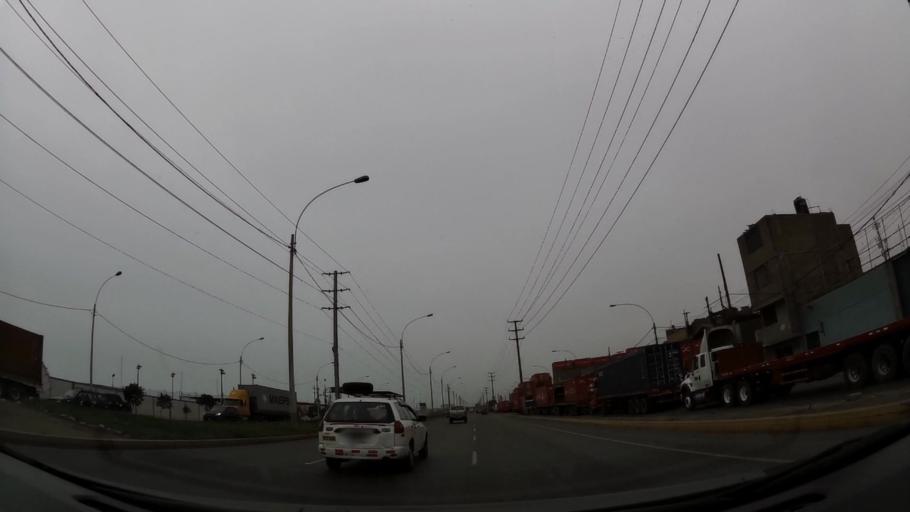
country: PE
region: Lima
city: Ventanilla
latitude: -11.9586
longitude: -77.1285
